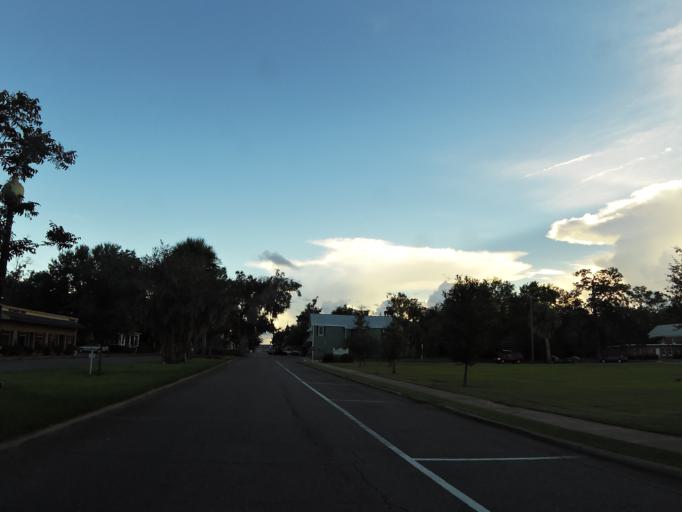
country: US
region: Georgia
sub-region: Camden County
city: St. Marys
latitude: 30.7239
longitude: -81.5478
